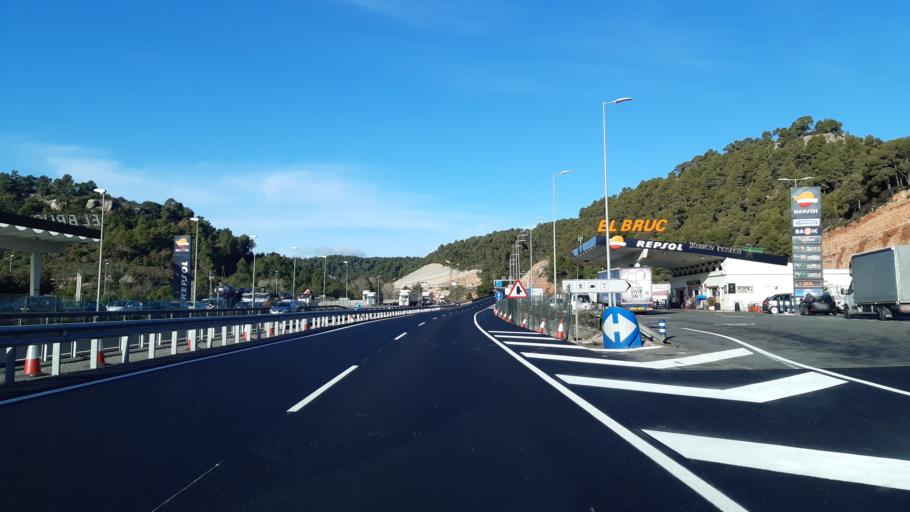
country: ES
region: Catalonia
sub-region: Provincia de Barcelona
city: Castelloli
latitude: 41.5932
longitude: 1.7515
